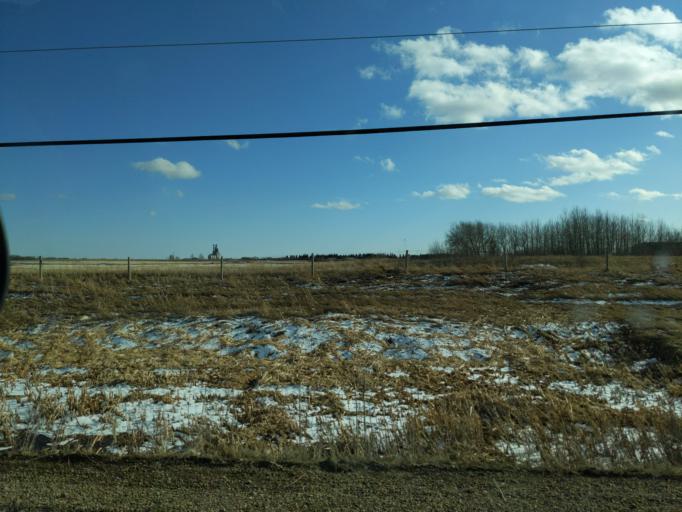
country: CA
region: Saskatchewan
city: Lloydminster
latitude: 53.2752
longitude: -109.9767
